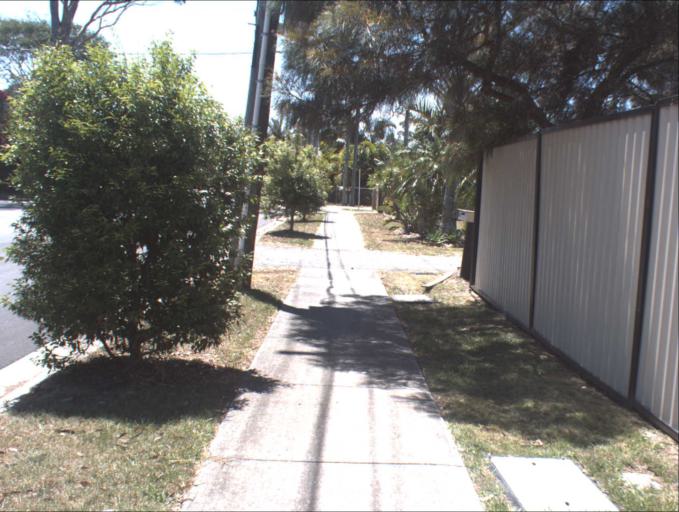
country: AU
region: Queensland
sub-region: Logan
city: Beenleigh
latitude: -27.6796
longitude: 153.1839
